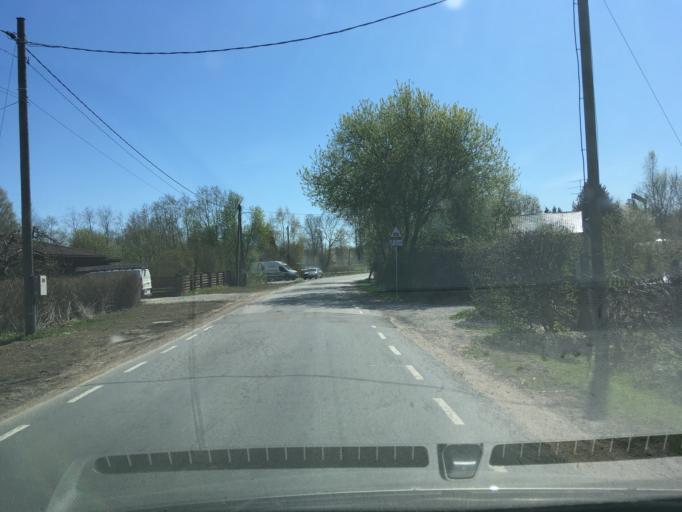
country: EE
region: Harju
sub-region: Raasiku vald
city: Arukula
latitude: 59.3732
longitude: 25.0787
